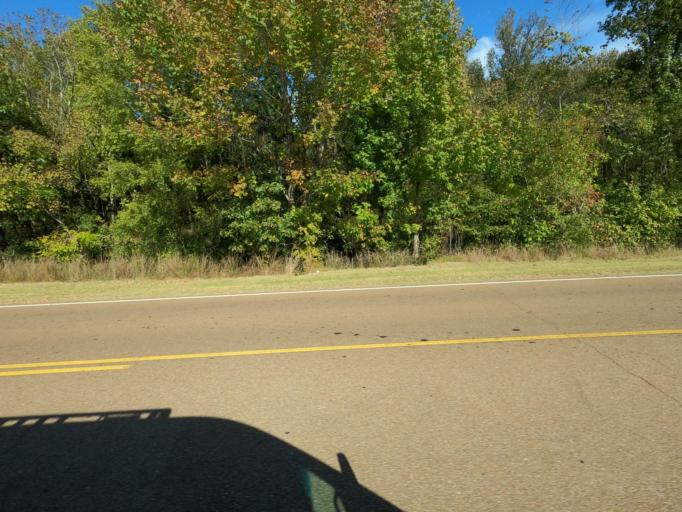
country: US
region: Tennessee
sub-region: Shelby County
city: Arlington
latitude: 35.2536
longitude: -89.6554
